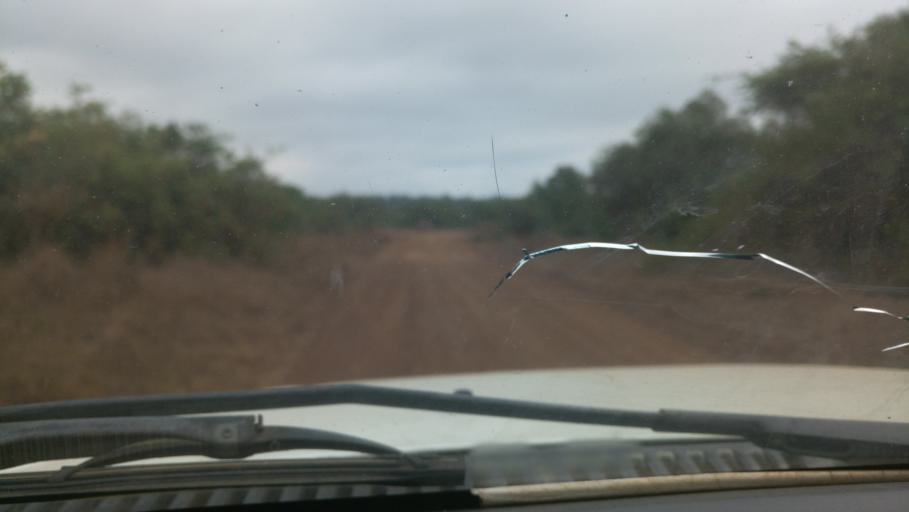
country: KE
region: Nairobi Area
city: Nairobi
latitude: -1.3694
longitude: 36.7789
